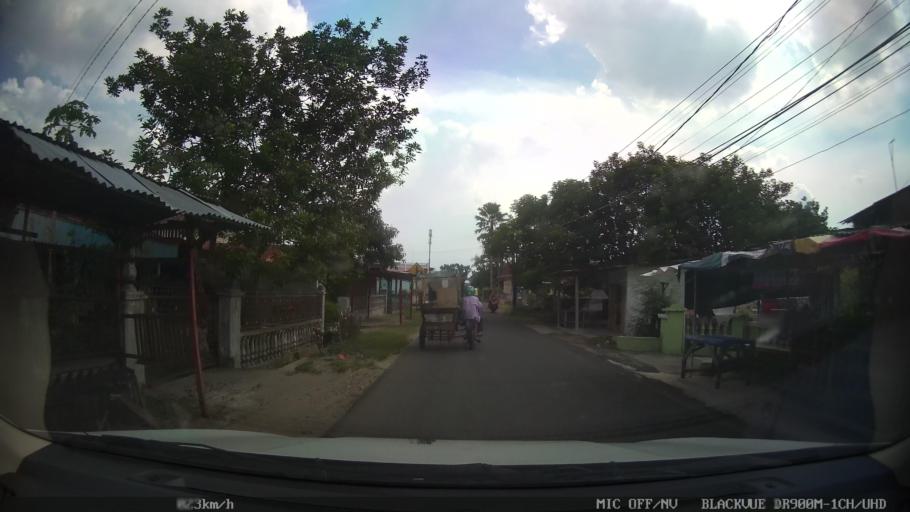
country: ID
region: North Sumatra
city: Binjai
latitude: 3.6148
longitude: 98.4993
